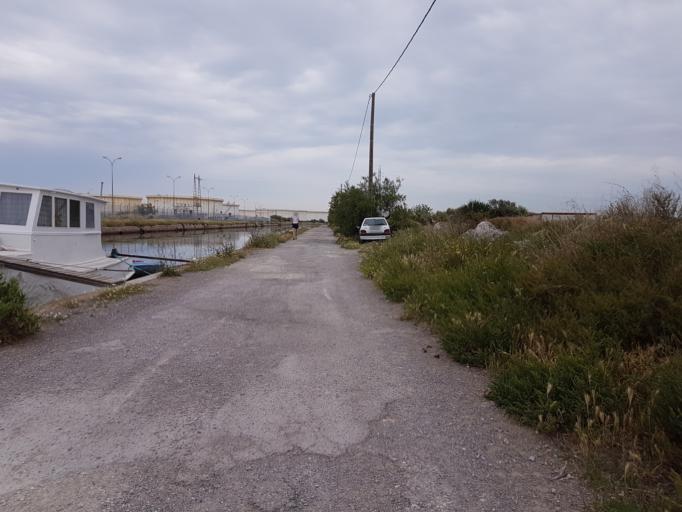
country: FR
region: Languedoc-Roussillon
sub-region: Departement de l'Herault
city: Frontignan
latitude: 43.4383
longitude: 3.7528
